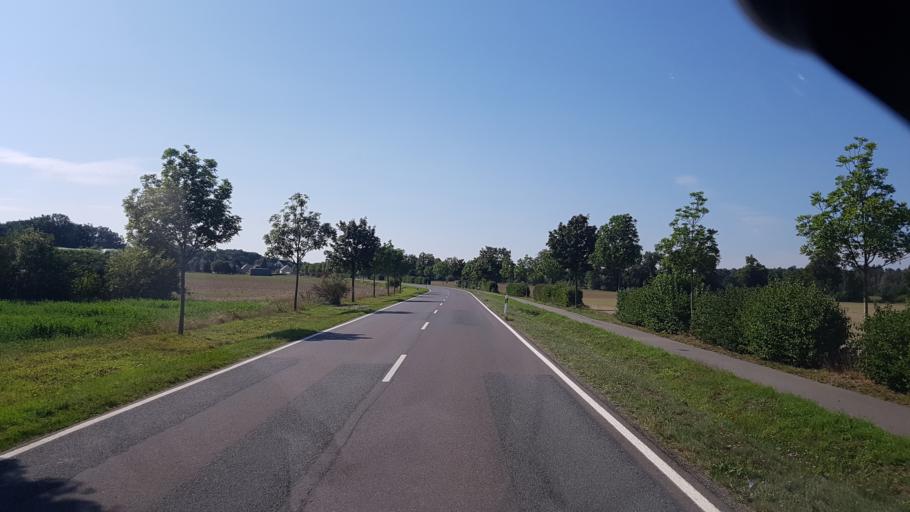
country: DE
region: Brandenburg
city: Altdobern
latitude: 51.7196
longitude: 14.0404
